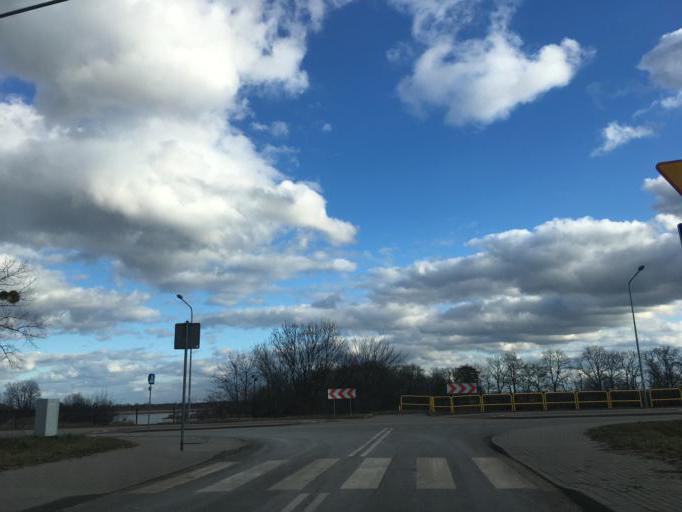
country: PL
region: Pomeranian Voivodeship
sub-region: Powiat gdanski
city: Cedry Wielkie
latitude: 54.3098
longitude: 18.9245
